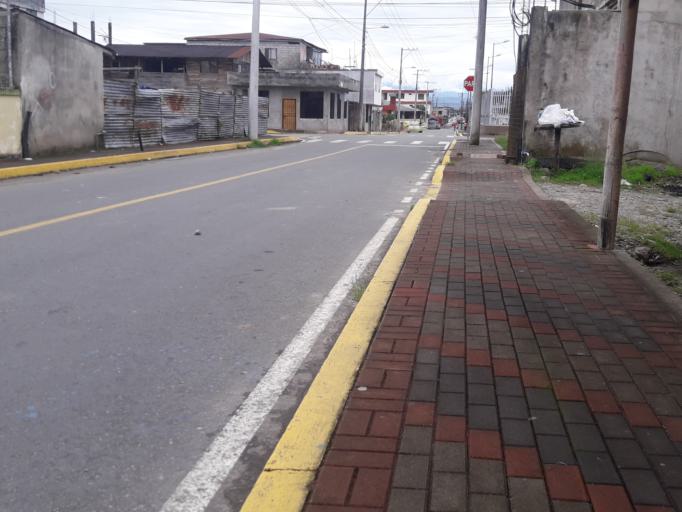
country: EC
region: Napo
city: Tena
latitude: -1.0054
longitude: -77.8123
